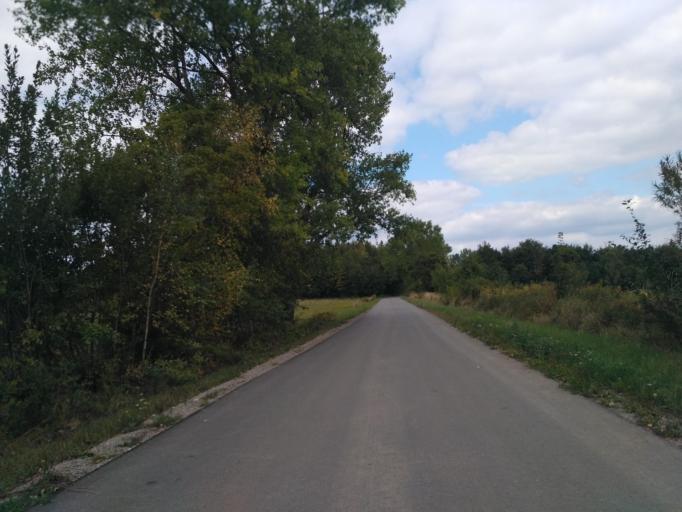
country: PL
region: Subcarpathian Voivodeship
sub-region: Powiat rzeszowski
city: Dynow
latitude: 49.7750
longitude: 22.2794
